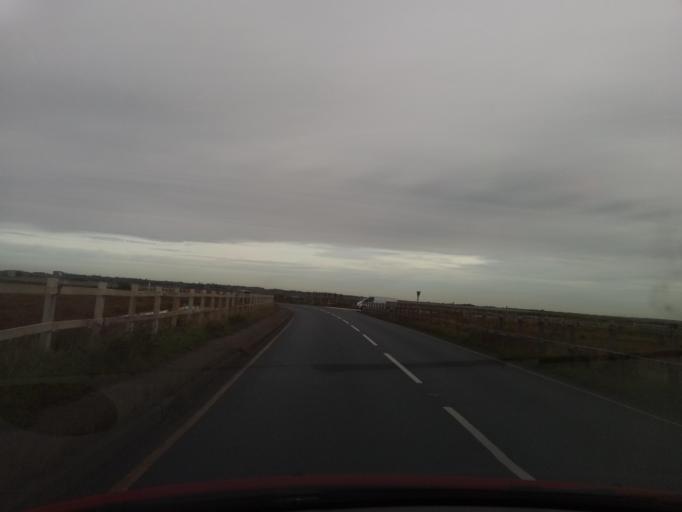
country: GB
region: England
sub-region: Essex
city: West Mersea
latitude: 51.7949
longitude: 0.9214
